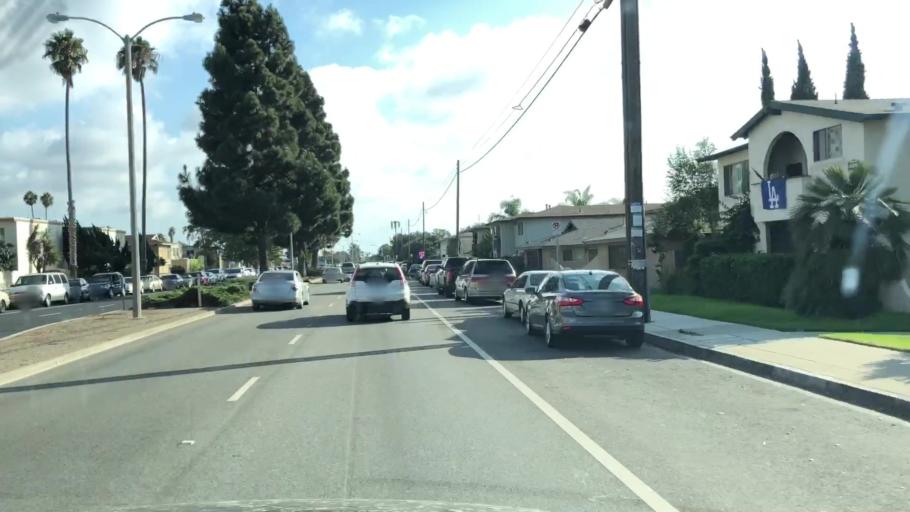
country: US
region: California
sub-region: Ventura County
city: Oxnard
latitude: 34.2229
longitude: -119.1946
